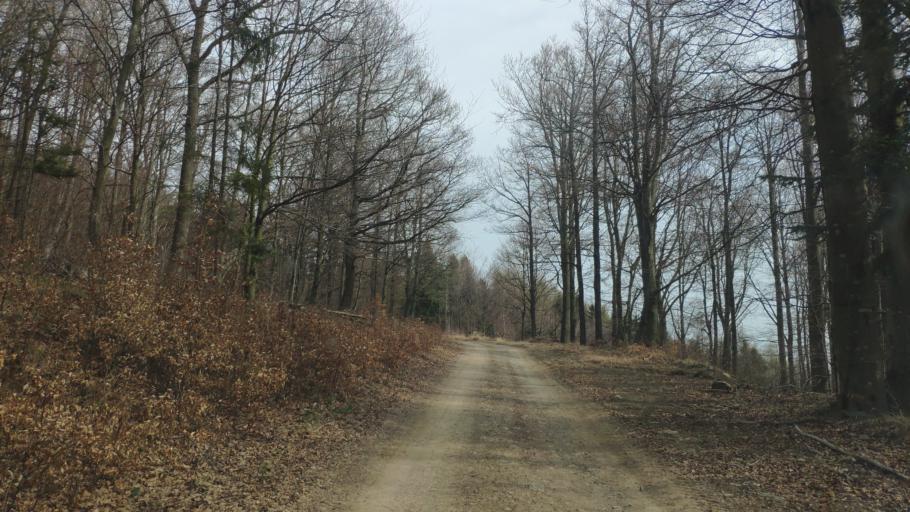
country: SK
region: Kosicky
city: Moldava nad Bodvou
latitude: 48.7409
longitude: 21.0437
